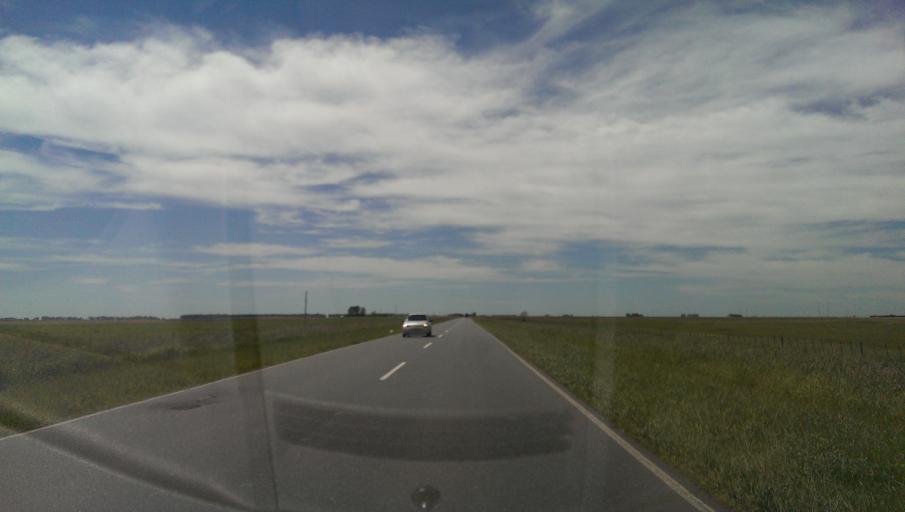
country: AR
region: Buenos Aires
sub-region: Partido de Laprida
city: Laprida
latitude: -37.3136
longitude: -60.8951
